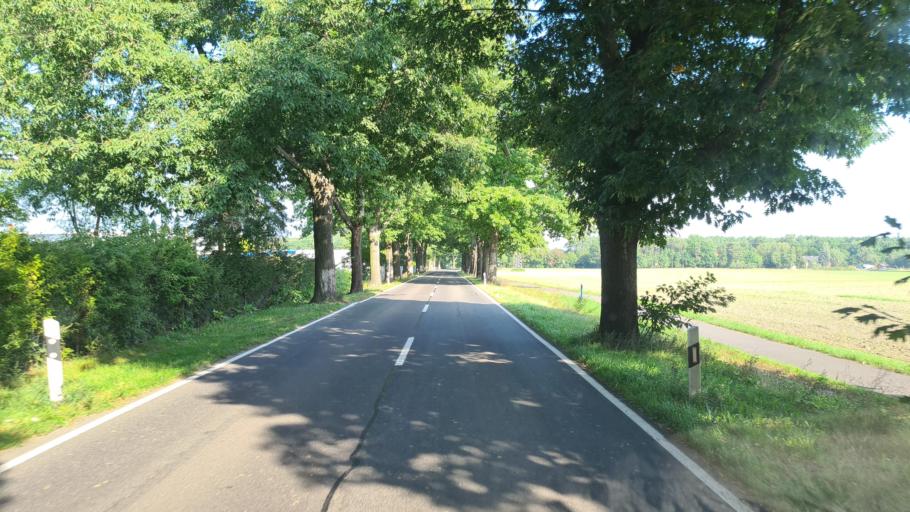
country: DE
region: Brandenburg
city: Kolkwitz
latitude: 51.7358
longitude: 14.2600
